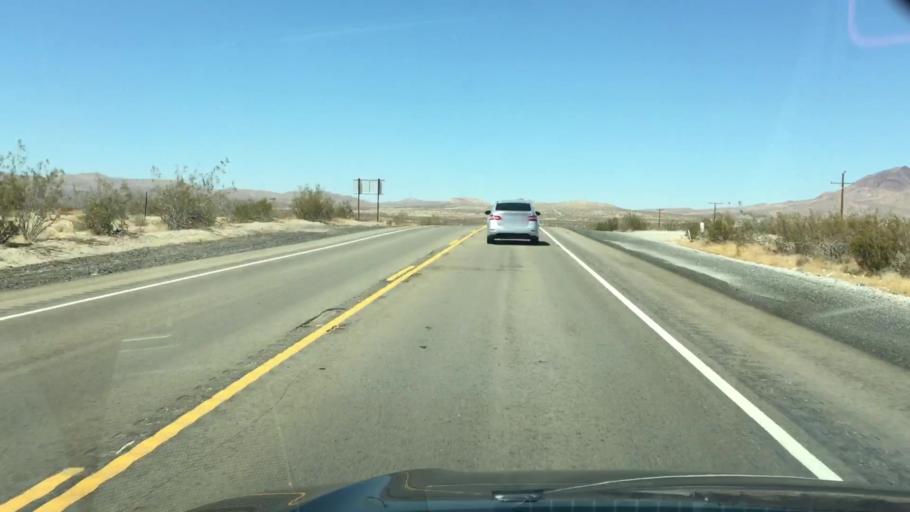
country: US
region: California
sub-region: Kern County
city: Boron
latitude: 35.2745
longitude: -117.6148
